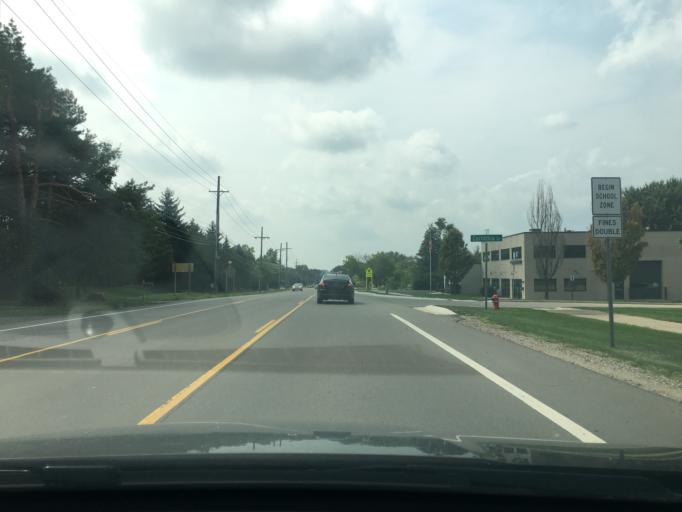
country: US
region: Michigan
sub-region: Oakland County
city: Rochester Hills
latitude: 42.6357
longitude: -83.1536
